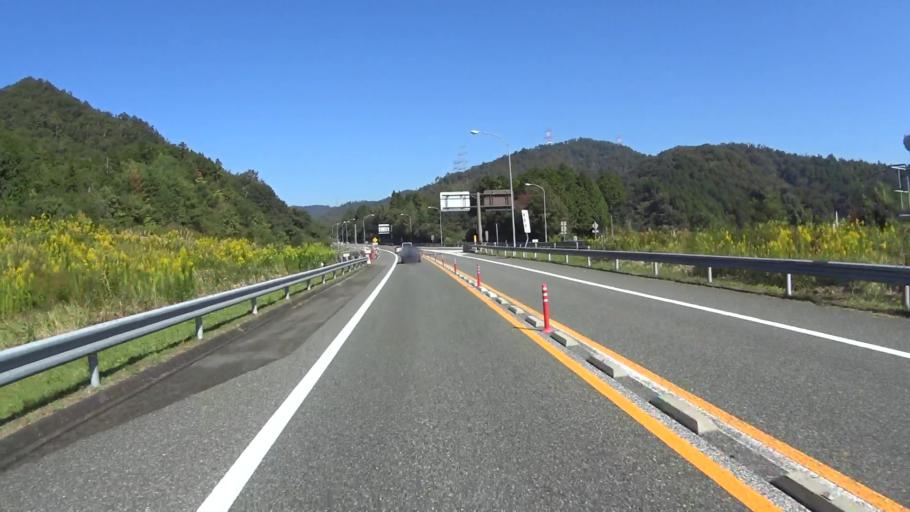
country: JP
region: Kyoto
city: Ayabe
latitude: 35.3560
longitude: 135.2890
